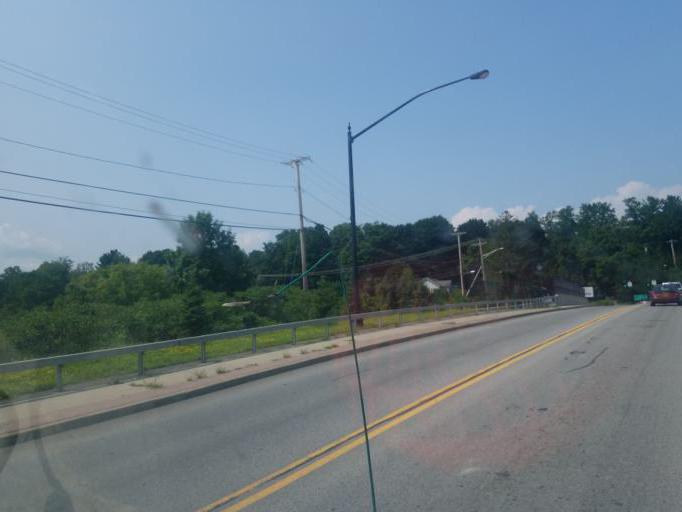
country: US
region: New York
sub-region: Montgomery County
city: Fonda
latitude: 42.9538
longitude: -74.3694
